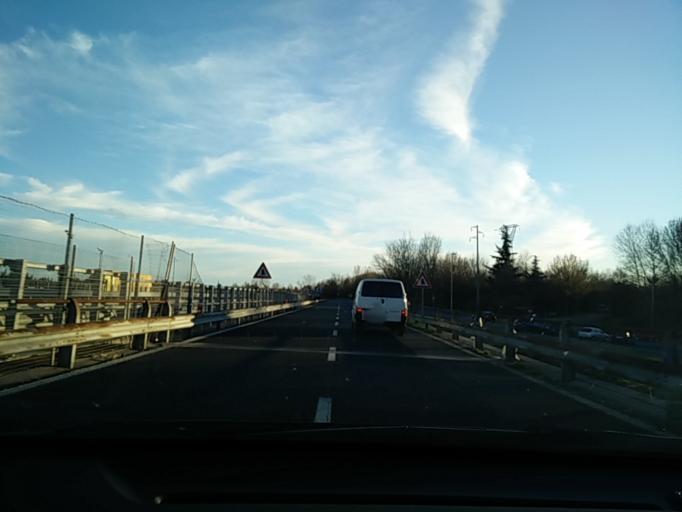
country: IT
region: Friuli Venezia Giulia
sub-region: Provincia di Udine
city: Colugna
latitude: 46.0853
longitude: 13.1921
